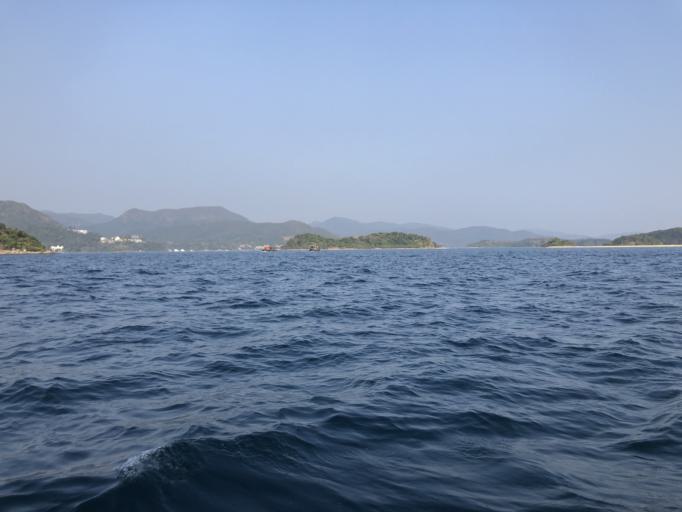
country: HK
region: Sai Kung
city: Sai Kung
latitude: 22.3759
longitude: 114.2801
